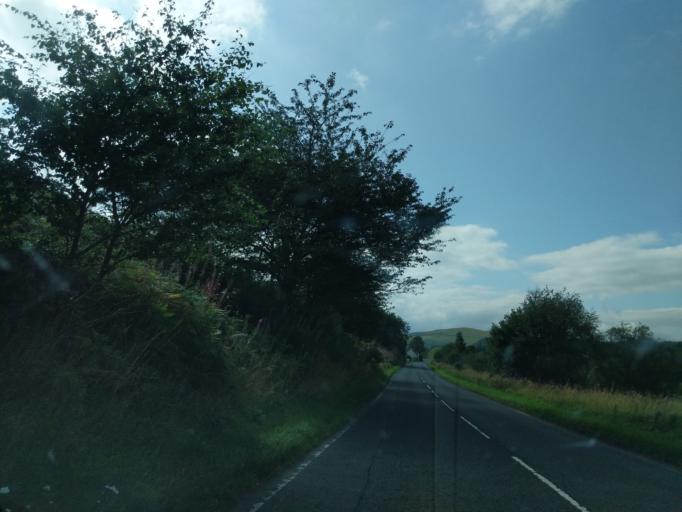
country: GB
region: Scotland
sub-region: The Scottish Borders
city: Peebles
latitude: 55.6948
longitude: -3.2128
